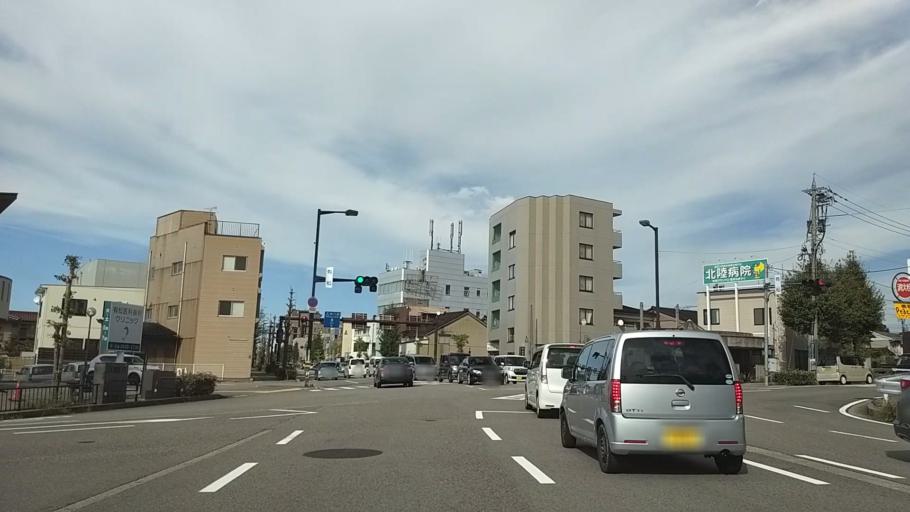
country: JP
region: Ishikawa
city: Nonoichi
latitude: 36.5443
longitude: 136.6412
